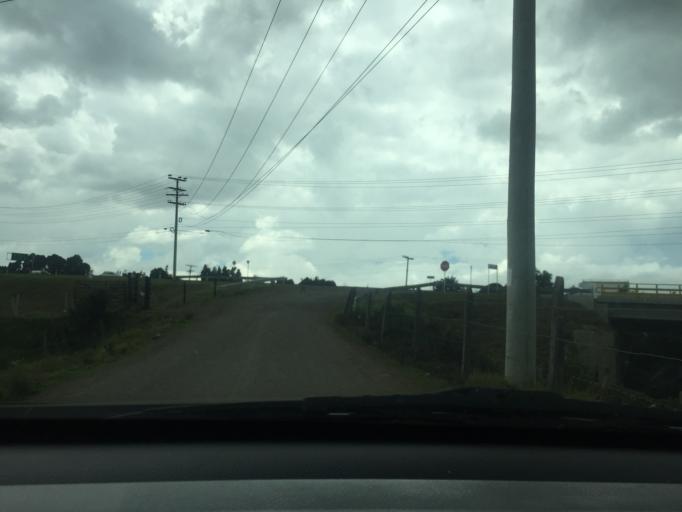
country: CO
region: Cundinamarca
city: Bojaca
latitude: 4.7766
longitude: -74.3181
